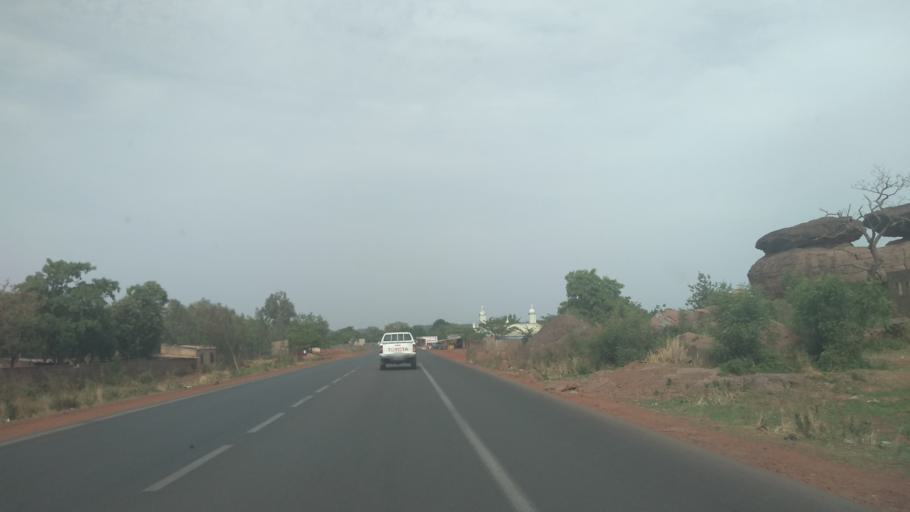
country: ML
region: Bamako
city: Bamako
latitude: 12.5794
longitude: -7.7827
